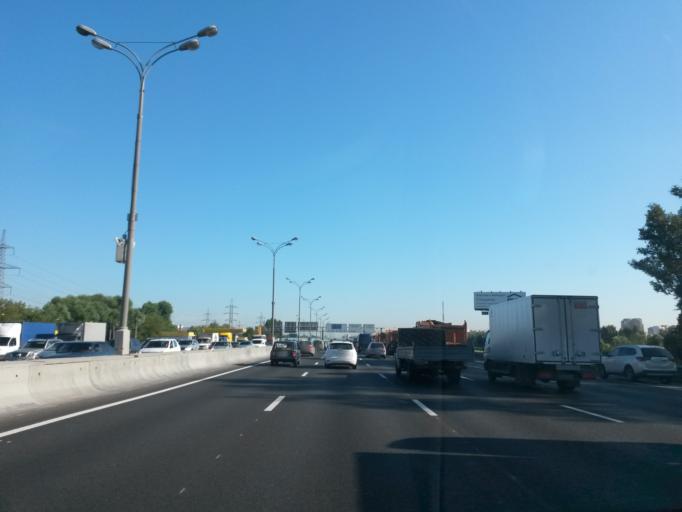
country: RU
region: Moskovskaya
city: Kuskovo
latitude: 55.7235
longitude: 37.8395
